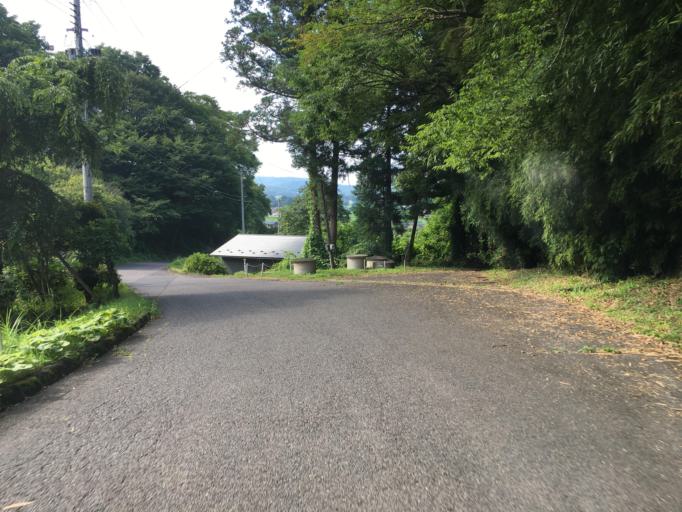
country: JP
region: Fukushima
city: Motomiya
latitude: 37.5531
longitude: 140.3980
